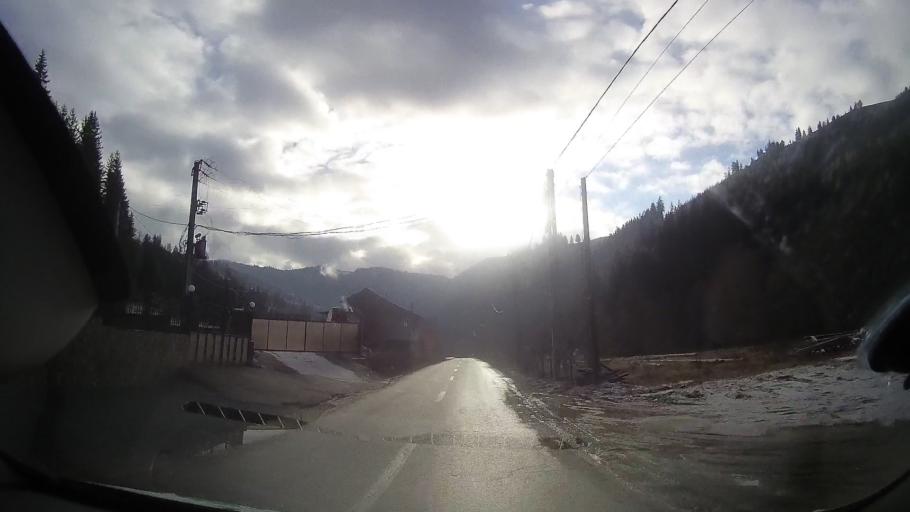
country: RO
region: Alba
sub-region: Comuna Albac
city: Albac
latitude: 46.4653
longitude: 22.9678
